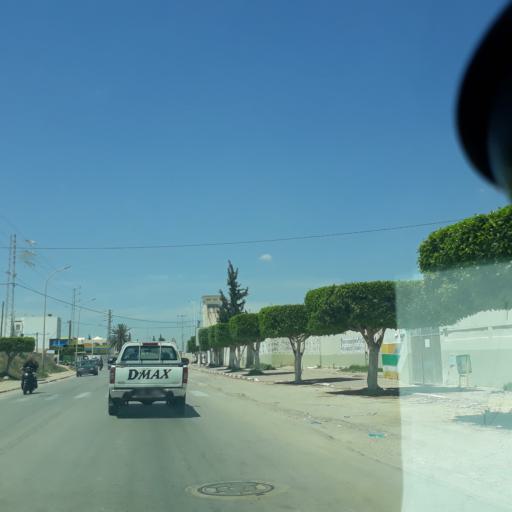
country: TN
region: Safaqis
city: Al Qarmadah
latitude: 34.8158
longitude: 10.7453
